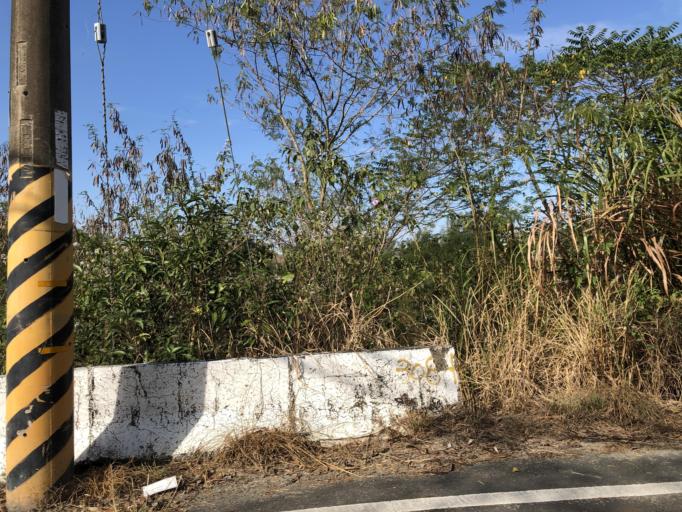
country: TW
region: Taiwan
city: Yujing
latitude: 23.0228
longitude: 120.3964
